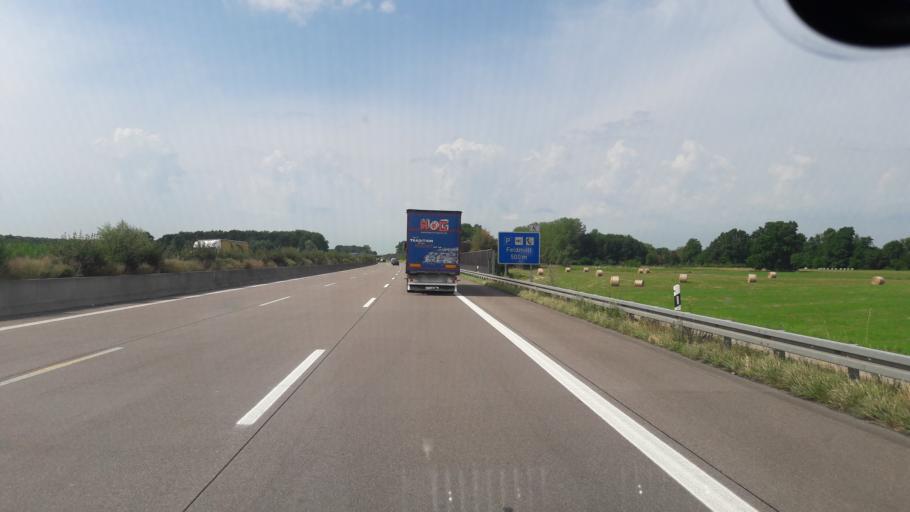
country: DE
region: Baden-Wuerttemberg
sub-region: Karlsruhe Region
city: Zell
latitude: 48.6664
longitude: 8.0447
